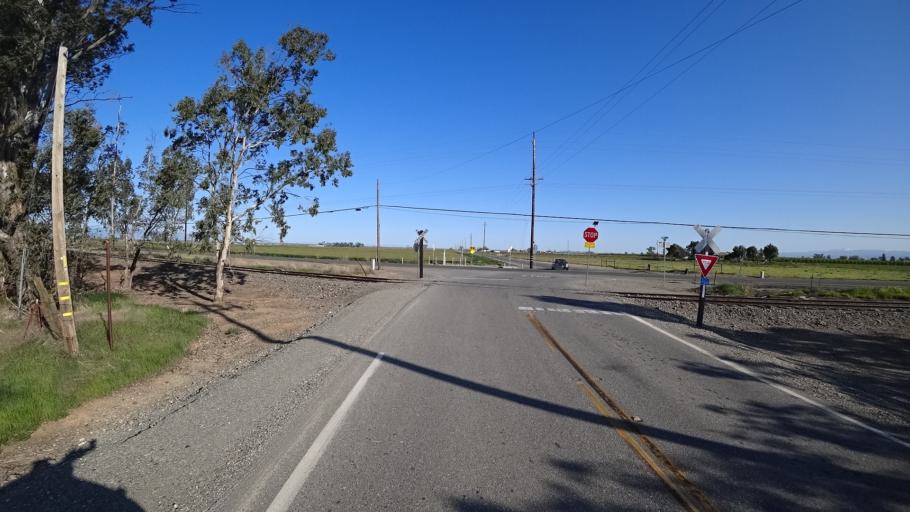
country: US
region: California
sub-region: Glenn County
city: Orland
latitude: 39.7682
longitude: -122.1099
